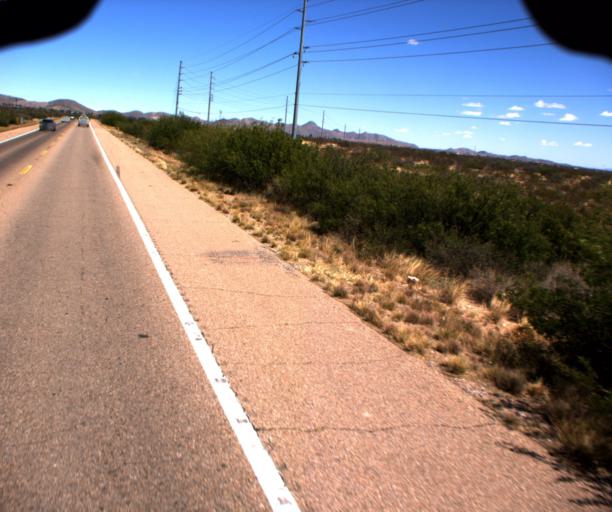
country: US
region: Arizona
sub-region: Cochise County
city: Naco
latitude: 31.3794
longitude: -109.9625
